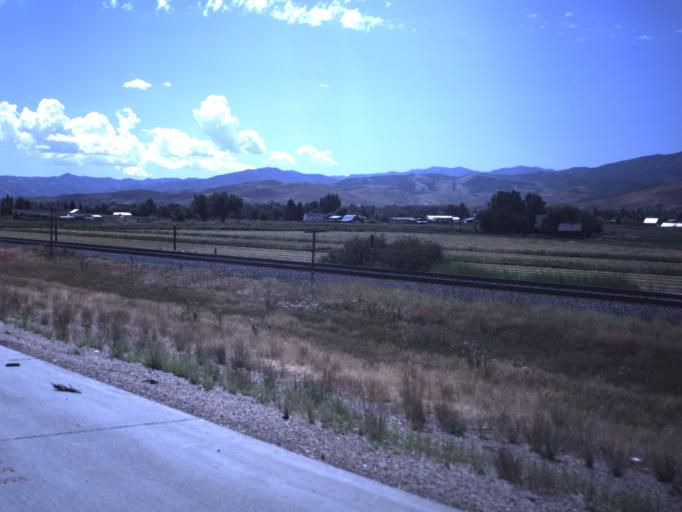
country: US
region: Utah
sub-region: Morgan County
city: Morgan
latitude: 41.0707
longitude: -111.7160
